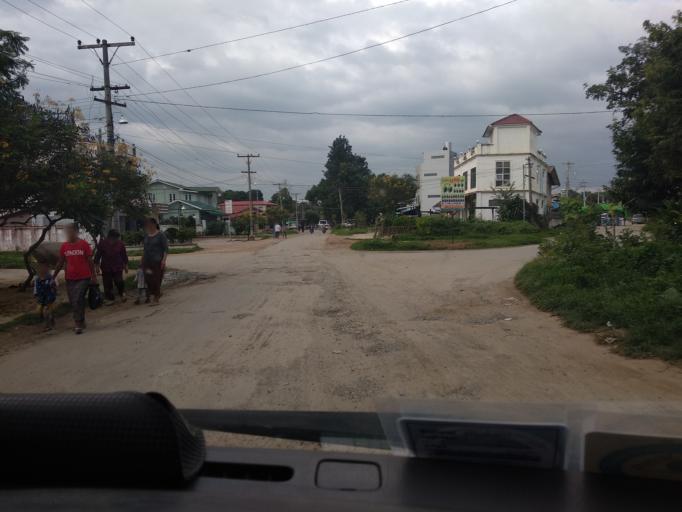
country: MM
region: Mandalay
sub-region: Pyin Oo Lwin District
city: Pyin Oo Lwin
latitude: 22.0335
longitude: 96.4782
